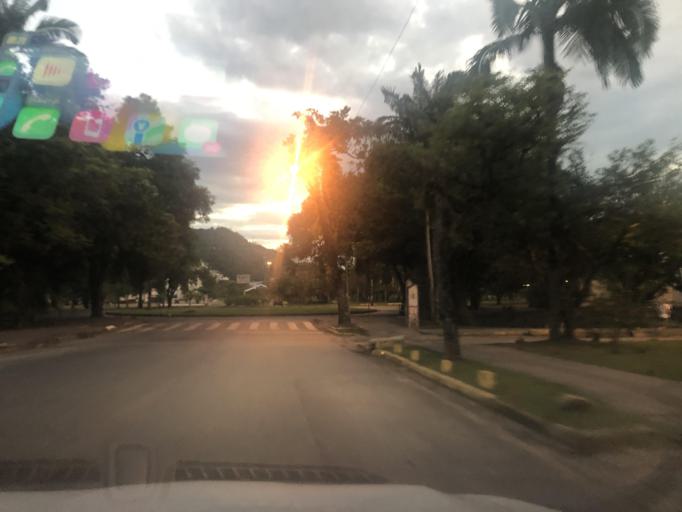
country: BR
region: Santa Catarina
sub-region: Florianopolis
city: Carvoeira
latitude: -27.5996
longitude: -48.5206
